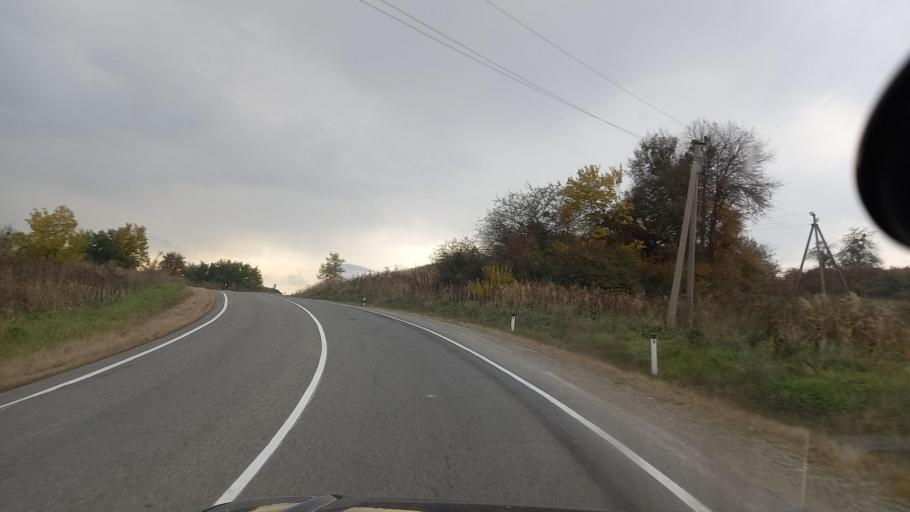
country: RU
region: Krasnodarskiy
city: Mostovskoy
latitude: 44.3803
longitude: 40.7385
